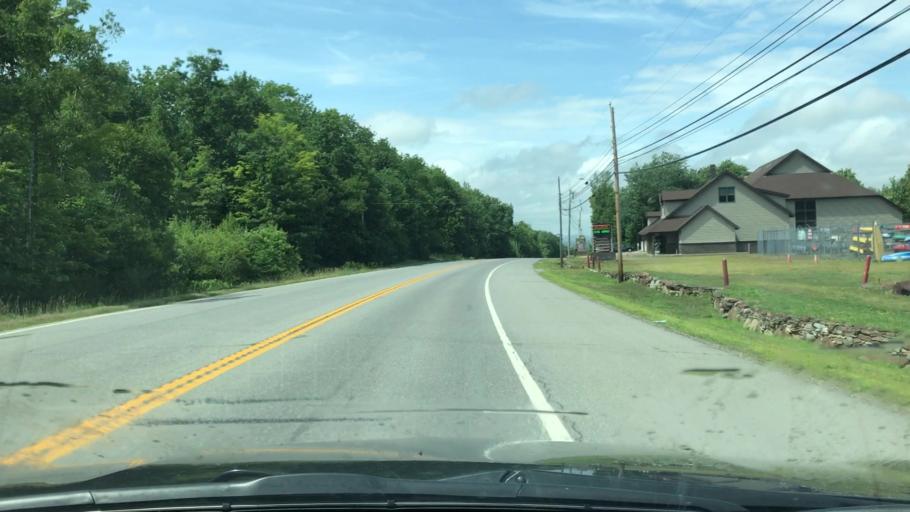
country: US
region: Maine
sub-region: Waldo County
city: Northport
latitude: 44.3602
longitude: -68.9746
